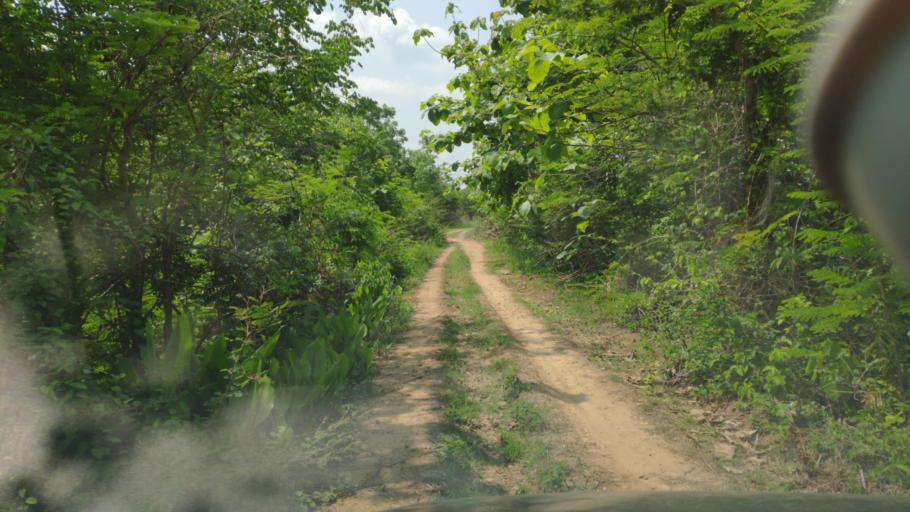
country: ID
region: Central Java
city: Gaplokan
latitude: -6.9139
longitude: 111.2643
